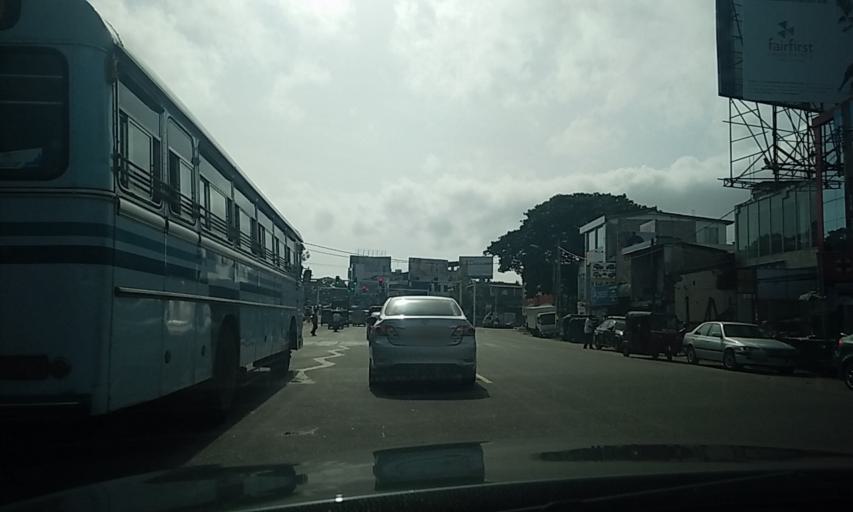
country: LK
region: Western
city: Sri Jayewardenepura Kotte
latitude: 6.8626
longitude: 79.9023
